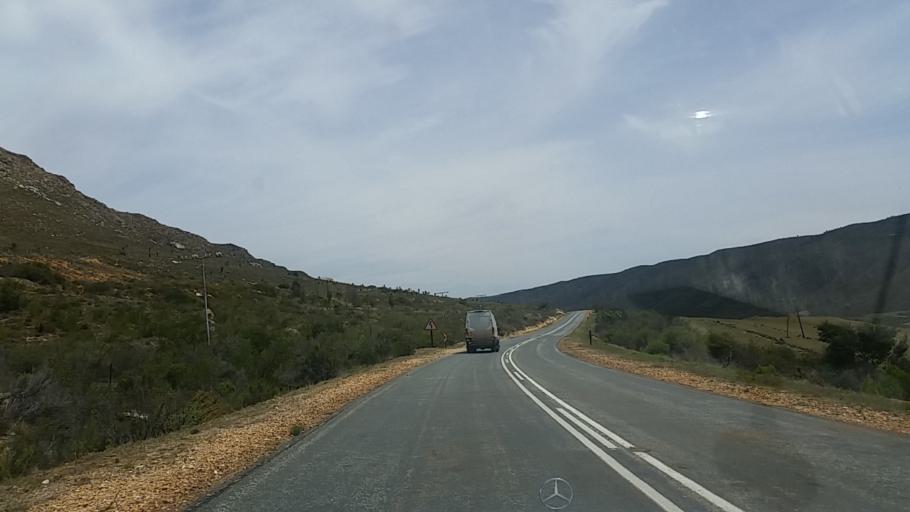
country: ZA
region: Western Cape
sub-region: Eden District Municipality
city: Knysna
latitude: -33.7425
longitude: 23.0300
